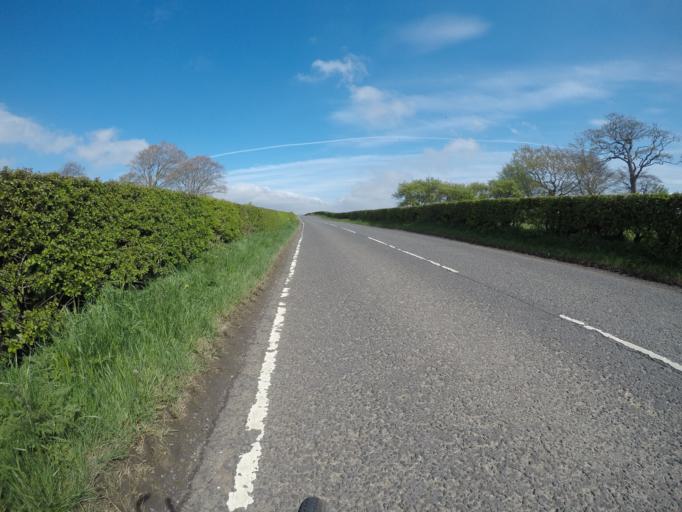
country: GB
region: Scotland
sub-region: East Ayrshire
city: Stewarton
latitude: 55.6680
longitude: -4.5340
